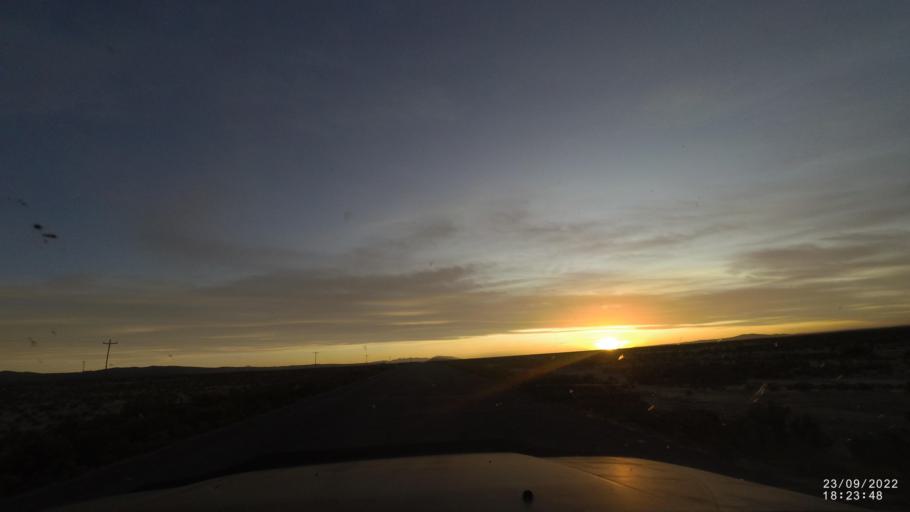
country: BO
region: Oruro
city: Challapata
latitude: -19.2978
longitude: -67.1096
